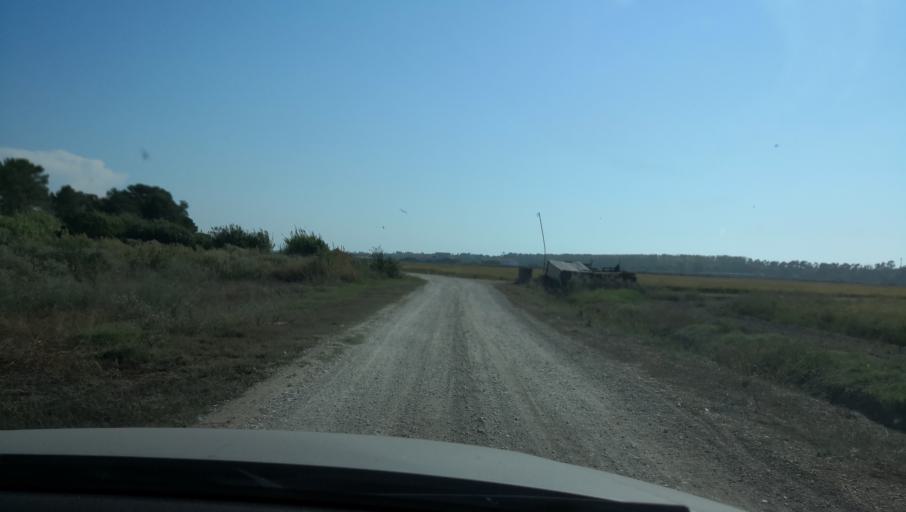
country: PT
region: Setubal
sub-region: Setubal
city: Setubal
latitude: 38.3900
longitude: -8.7897
